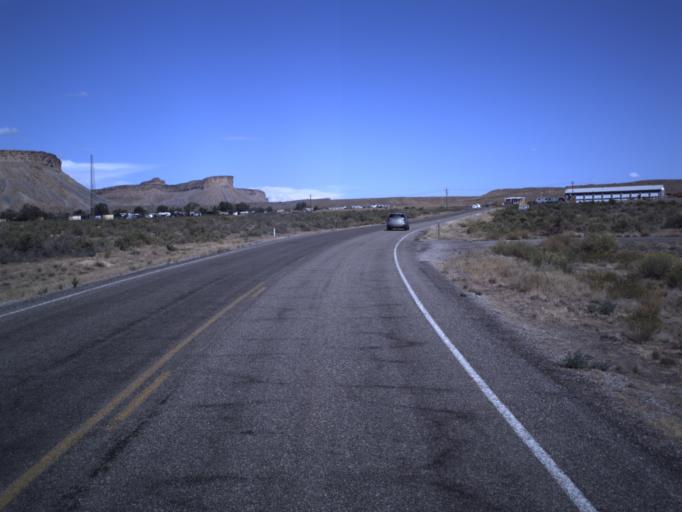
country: US
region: Utah
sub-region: Grand County
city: Moab
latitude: 38.9651
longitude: -109.7214
